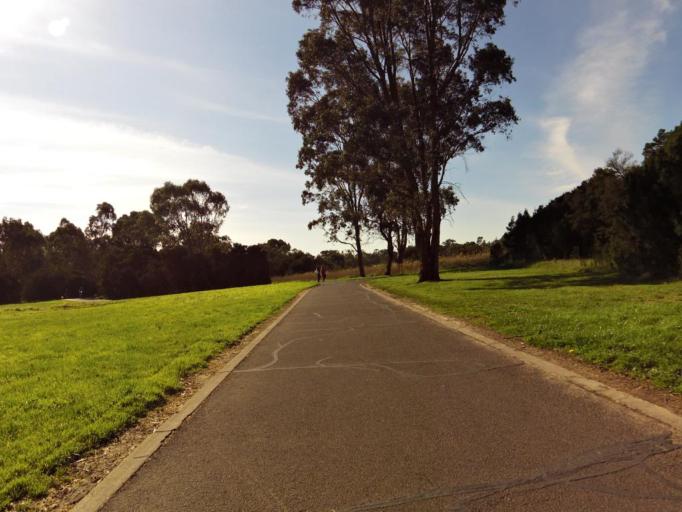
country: AU
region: Victoria
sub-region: Monash
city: Mulgrave
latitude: -37.9013
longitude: 145.2013
